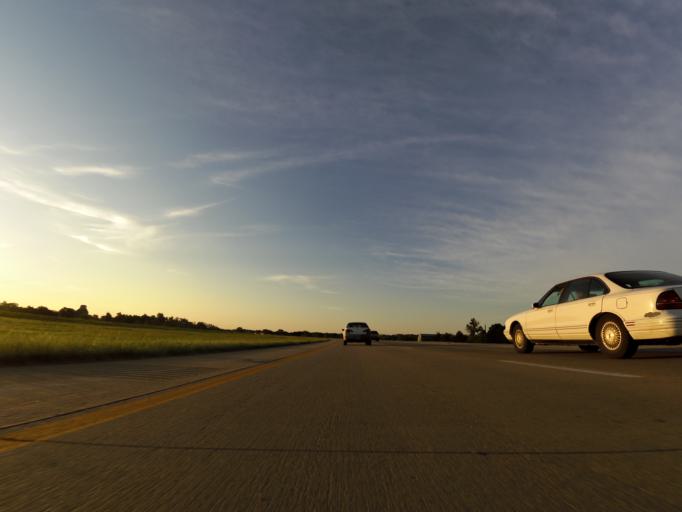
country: US
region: Kansas
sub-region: Reno County
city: South Hutchinson
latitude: 37.9713
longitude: -97.9368
